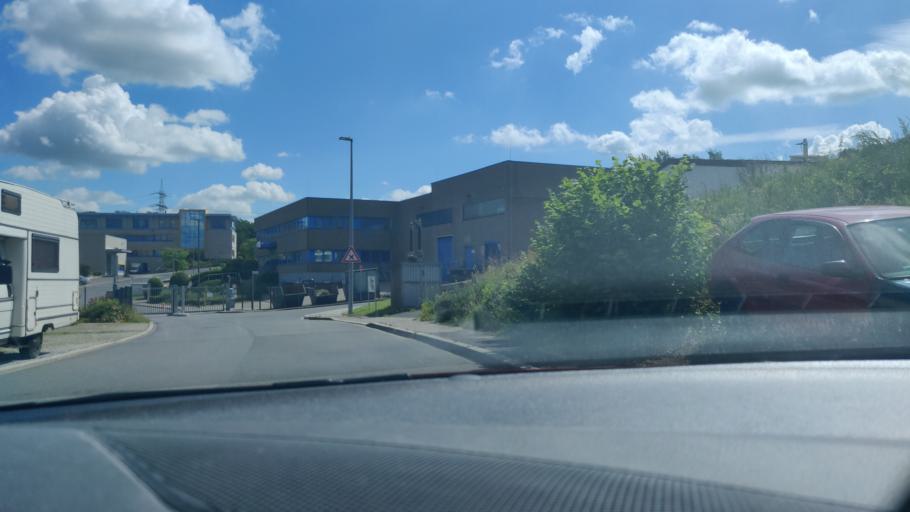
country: DE
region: North Rhine-Westphalia
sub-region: Regierungsbezirk Dusseldorf
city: Heiligenhaus
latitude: 51.3351
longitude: 6.9982
